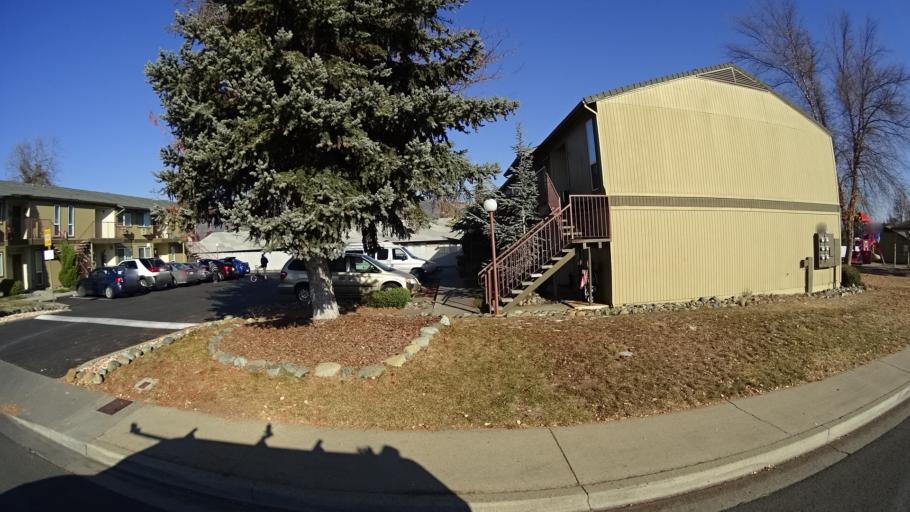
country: US
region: California
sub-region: Siskiyou County
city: Yreka
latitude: 41.7233
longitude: -122.6436
